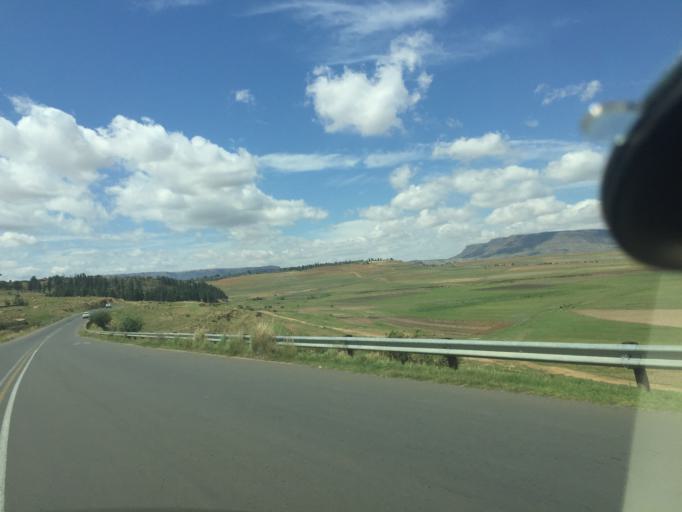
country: LS
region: Maseru
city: Maseru
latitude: -29.5137
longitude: 27.5239
